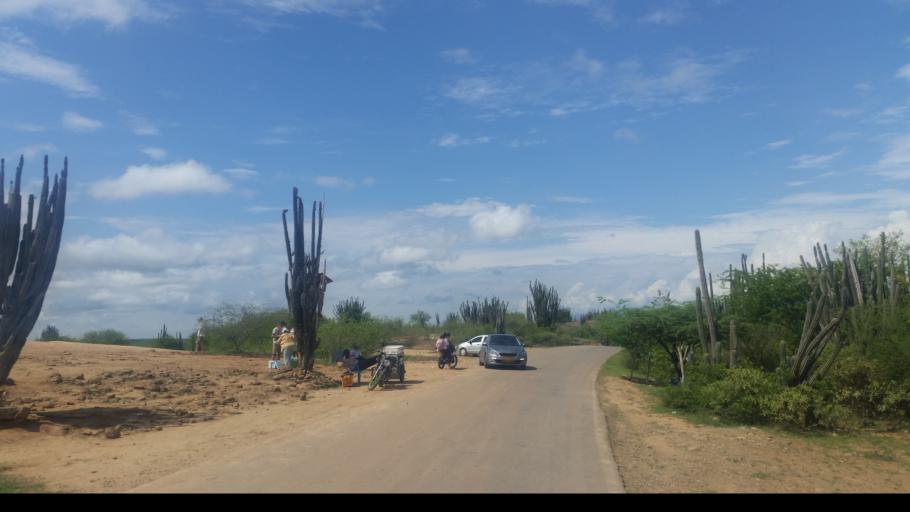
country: CO
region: Huila
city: Villavieja
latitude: 3.2297
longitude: -75.1811
